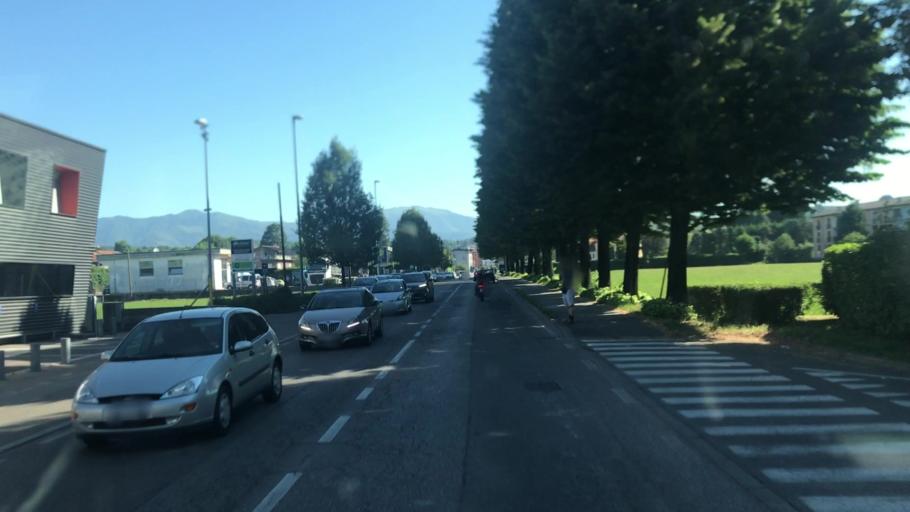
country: IT
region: Lombardy
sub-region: Provincia di Como
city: Cantu
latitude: 45.7424
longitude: 9.1201
